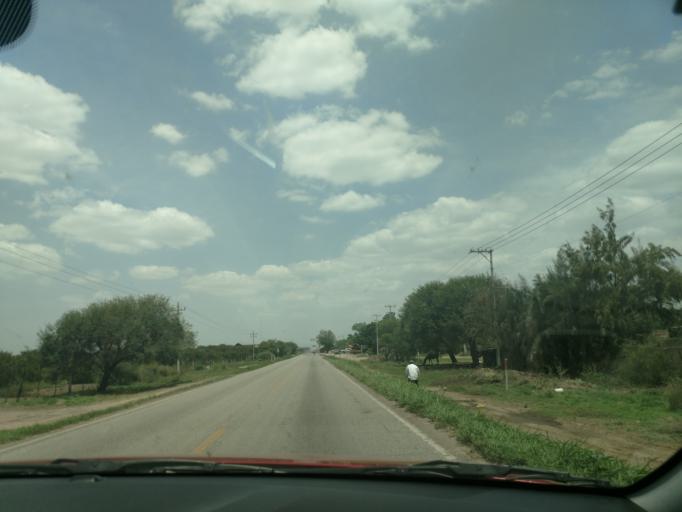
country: MX
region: San Luis Potosi
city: Ciudad Fernandez
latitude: 21.9484
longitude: -100.0585
